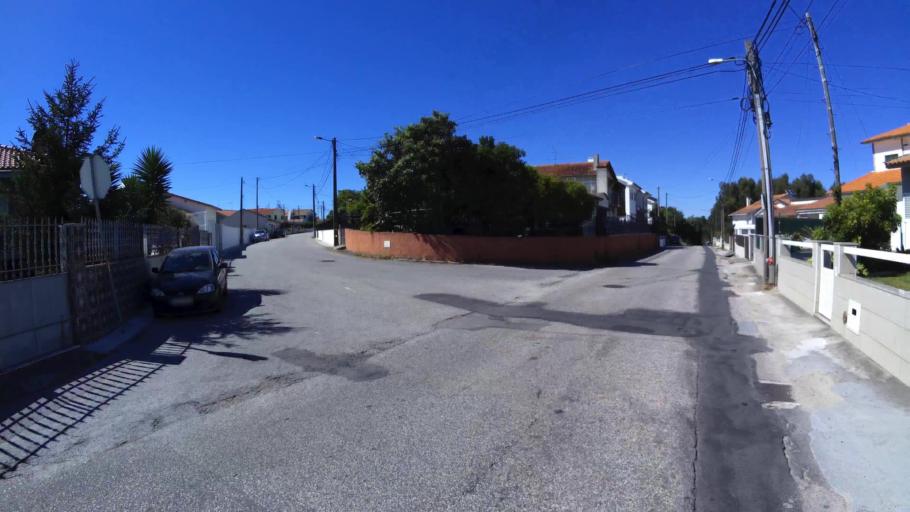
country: PT
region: Aveiro
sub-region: Aveiro
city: Aveiro
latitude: 40.6605
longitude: -8.6218
